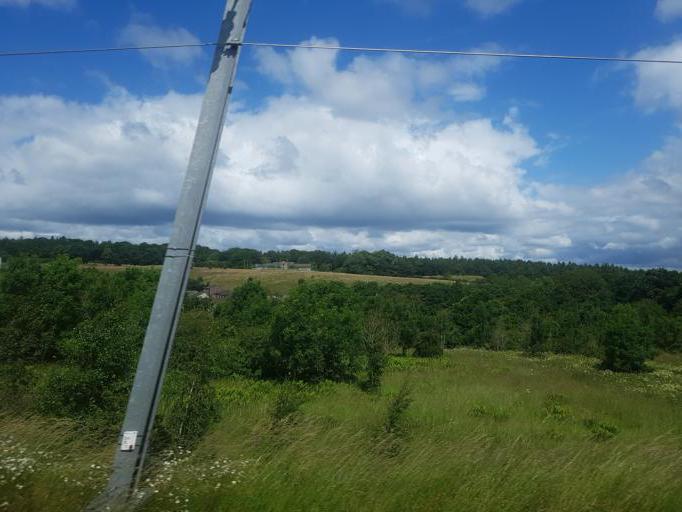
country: GB
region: Scotland
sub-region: Falkirk
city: Falkirk
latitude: 55.9837
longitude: -3.7616
